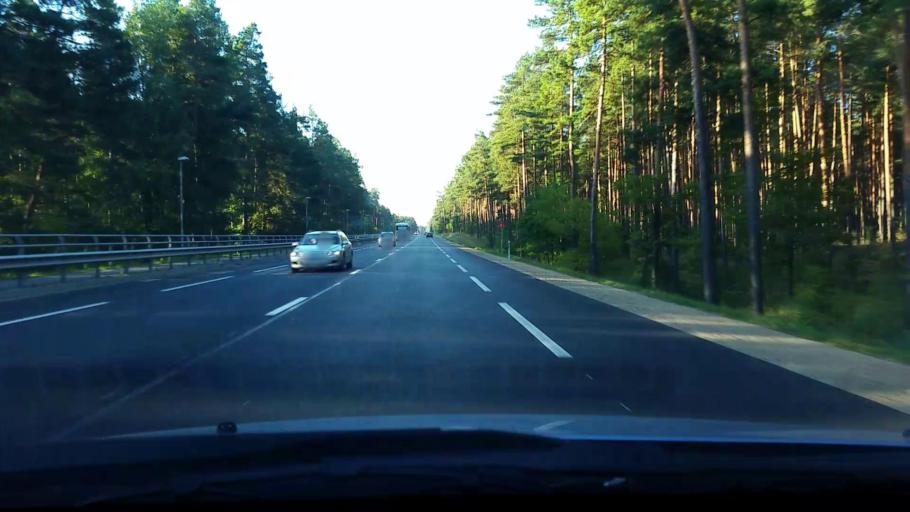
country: LV
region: Adazi
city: Adazi
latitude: 57.0563
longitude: 24.3209
